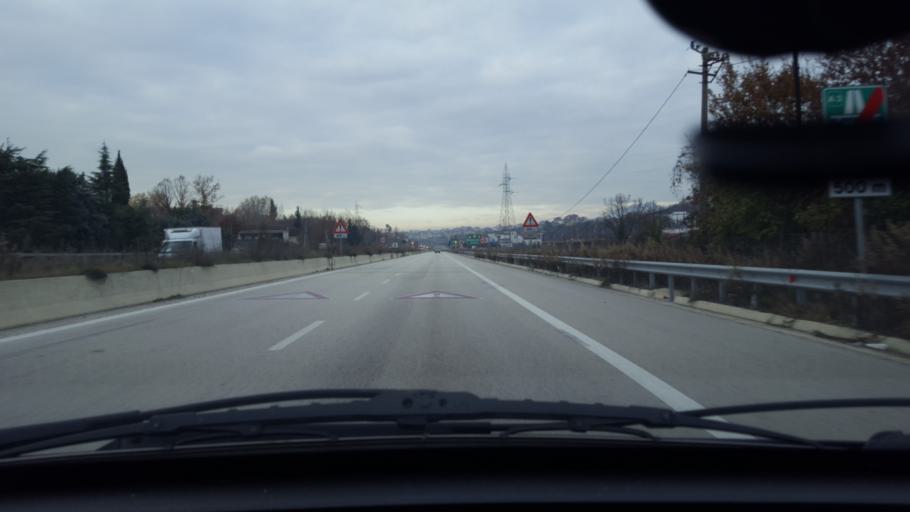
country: AL
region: Tirane
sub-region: Rrethi i Tiranes
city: Petrele
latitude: 41.2789
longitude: 19.8554
